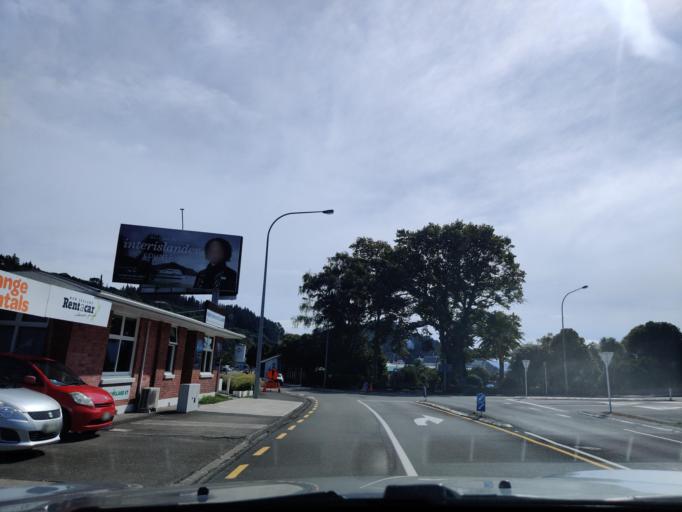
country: NZ
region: Marlborough
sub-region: Marlborough District
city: Picton
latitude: -41.2892
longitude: 174.0055
